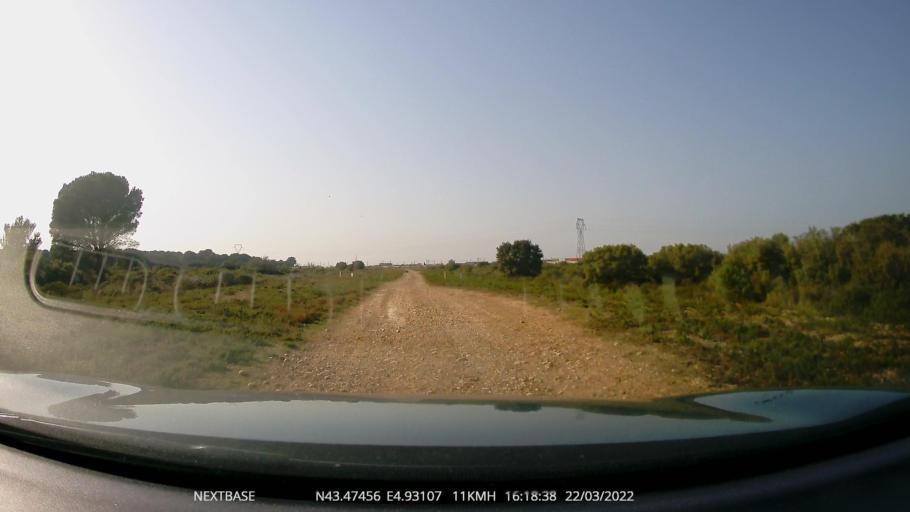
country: FR
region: Provence-Alpes-Cote d'Azur
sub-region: Departement des Bouches-du-Rhone
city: Fos-sur-Mer
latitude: 43.4746
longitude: 4.9311
